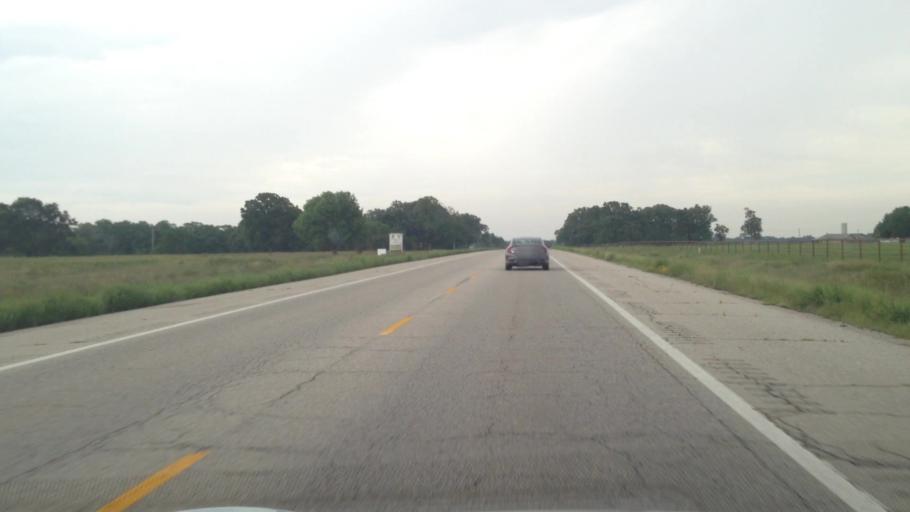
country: US
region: Kansas
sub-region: Cherokee County
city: Galena
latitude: 37.0162
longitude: -94.6343
